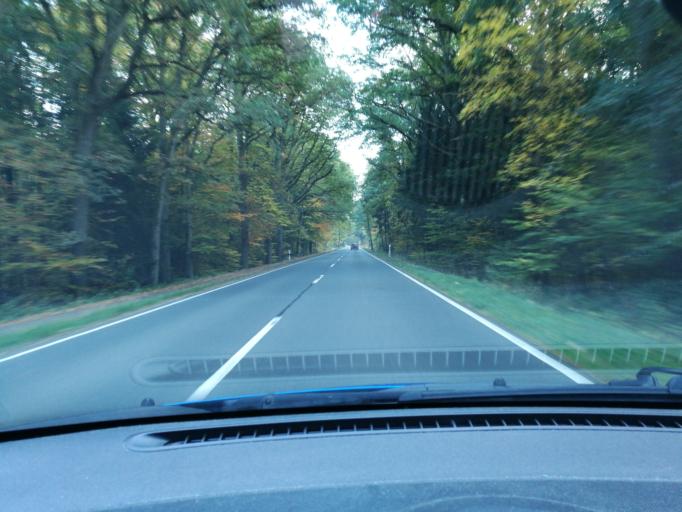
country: DE
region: Lower Saxony
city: Karwitz
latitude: 53.1166
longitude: 10.9957
